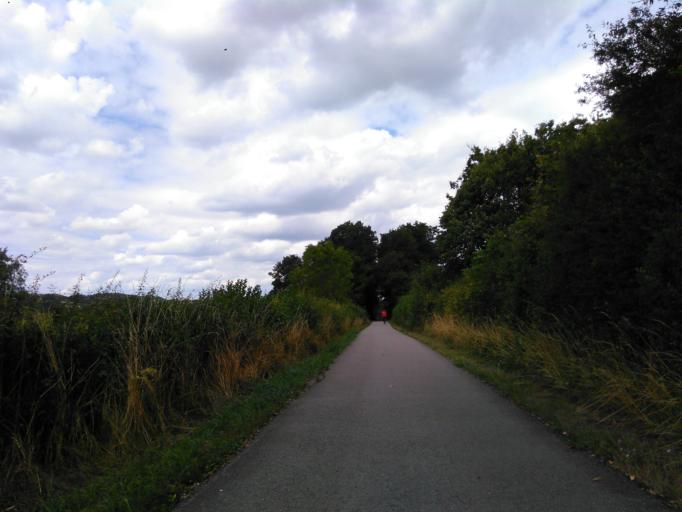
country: LU
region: Grevenmacher
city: Gonderange
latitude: 49.6818
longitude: 6.2502
